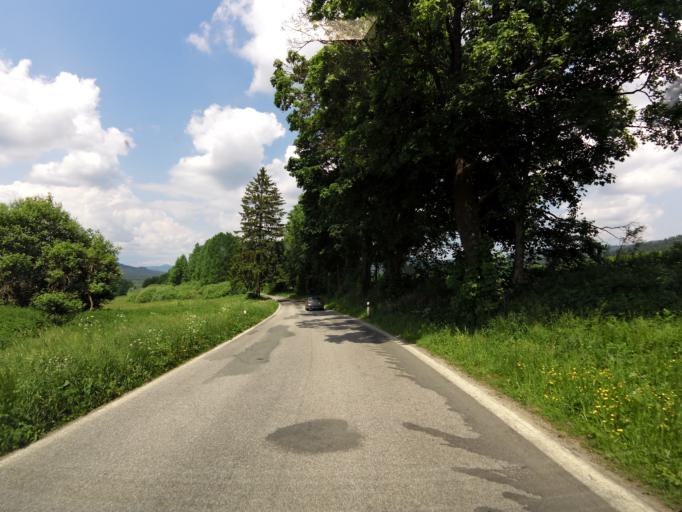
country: CZ
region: Jihocesky
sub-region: Okres Cesky Krumlov
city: Horni Plana
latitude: 48.8222
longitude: 13.9656
